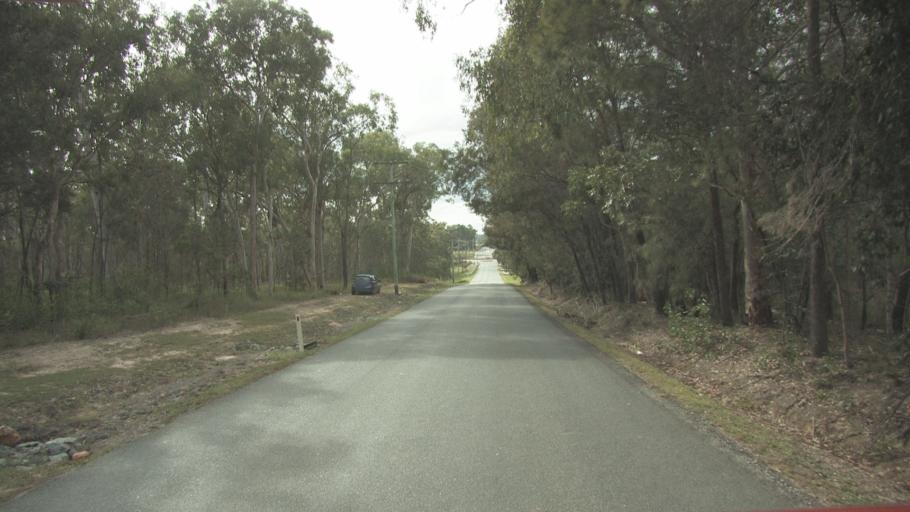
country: AU
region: Queensland
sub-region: Logan
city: Woodridge
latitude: -27.6535
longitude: 153.0847
